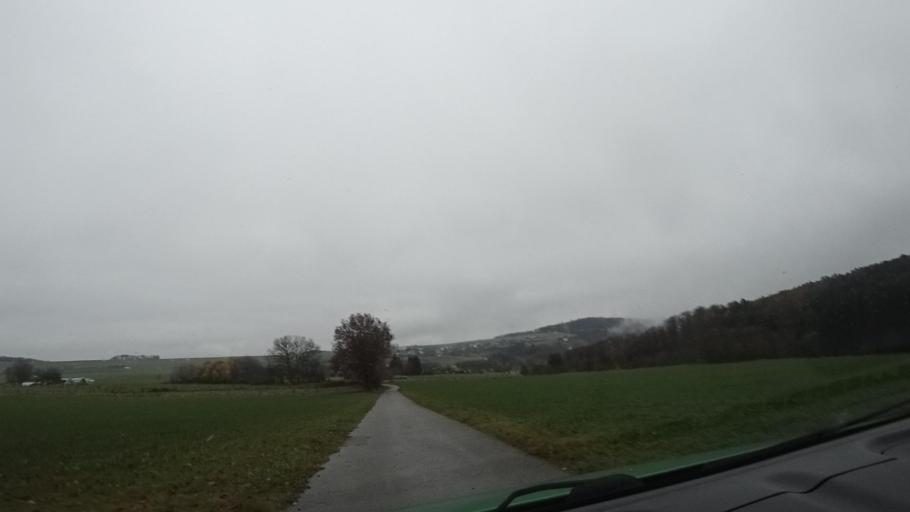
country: DE
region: Rheinland-Pfalz
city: Birkheim
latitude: 50.1121
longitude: 7.6163
